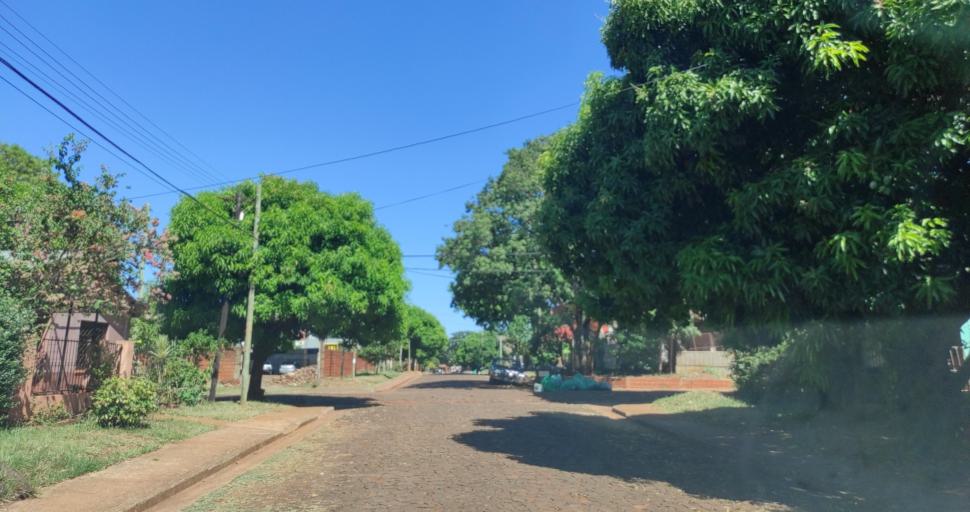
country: AR
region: Misiones
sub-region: Departamento de Capital
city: Posadas
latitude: -27.3895
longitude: -55.9279
